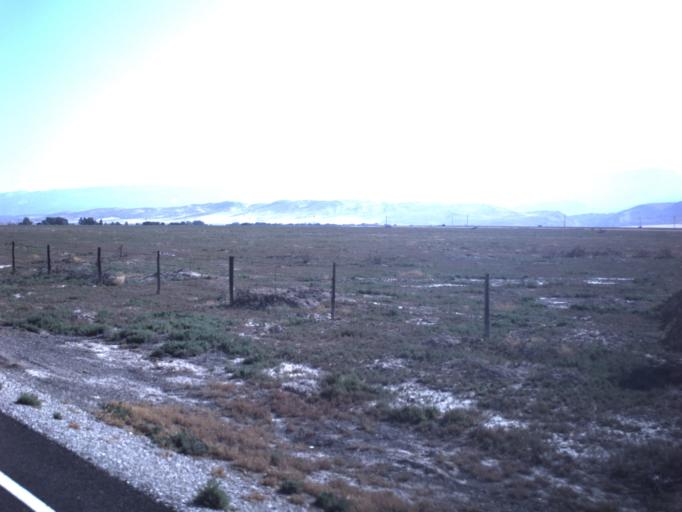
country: US
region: Utah
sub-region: Sevier County
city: Salina
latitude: 39.0313
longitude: -111.8413
